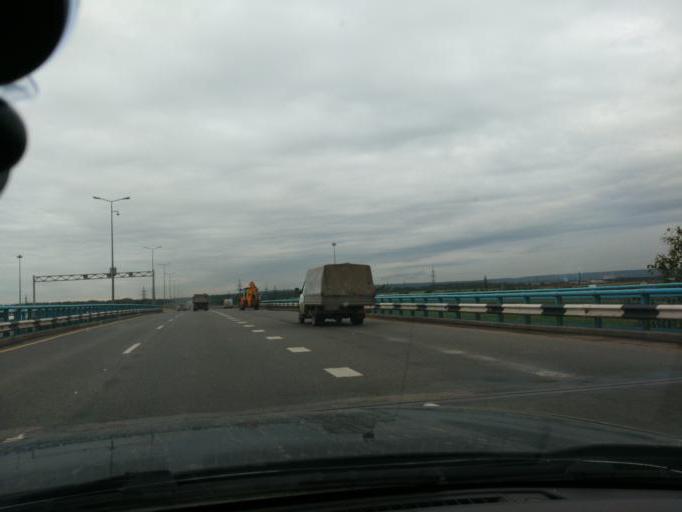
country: RU
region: Perm
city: Froly
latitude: 57.9329
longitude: 56.2665
